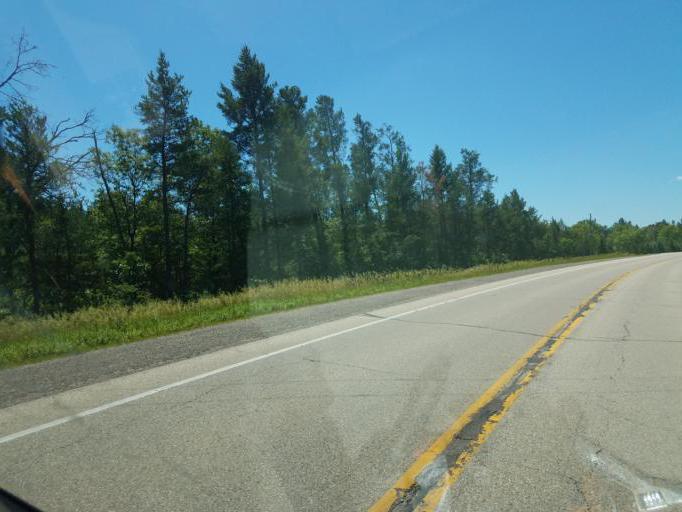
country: US
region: Wisconsin
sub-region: Juneau County
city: New Lisbon
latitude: 44.0434
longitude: -90.0263
